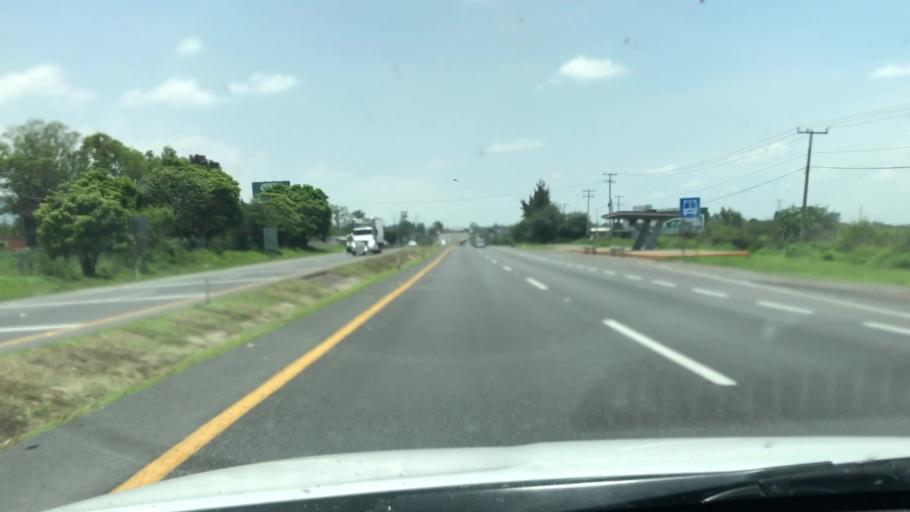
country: MX
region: Guanajuato
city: Penjamo
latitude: 20.4038
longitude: -101.7454
